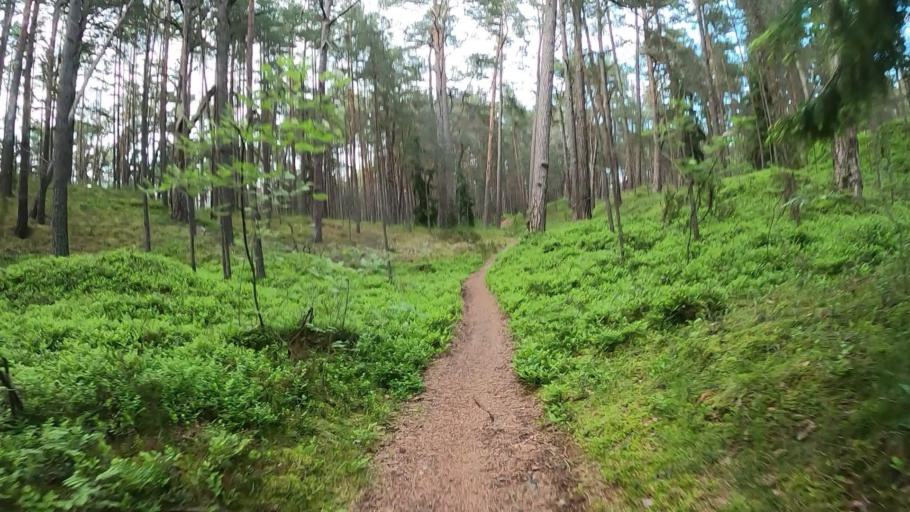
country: LV
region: Carnikava
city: Carnikava
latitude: 57.1213
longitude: 24.2095
